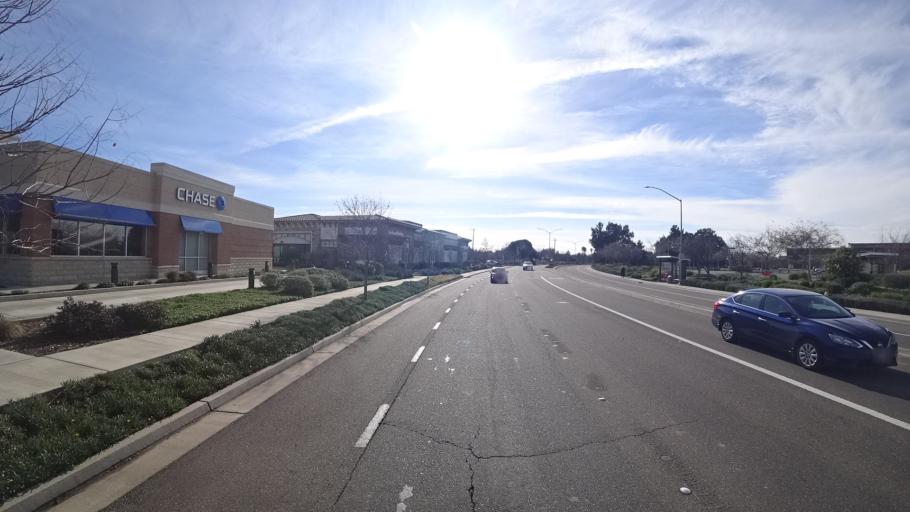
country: US
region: California
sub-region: Yolo County
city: Davis
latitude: 38.5540
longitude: -121.6973
